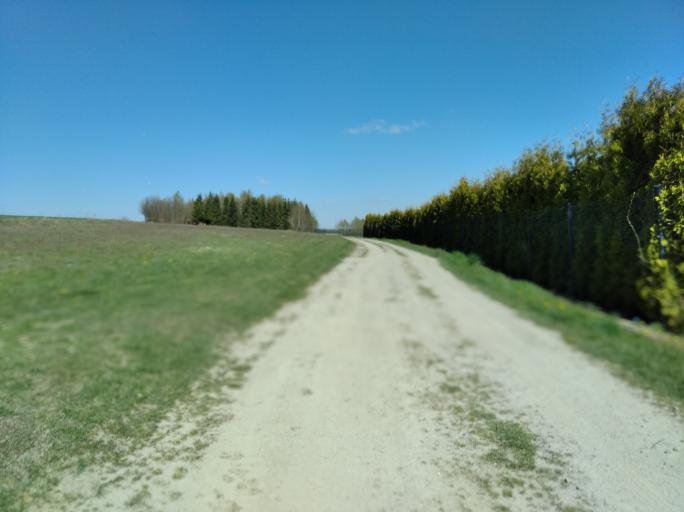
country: PL
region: Subcarpathian Voivodeship
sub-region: Powiat strzyzowski
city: Wisniowa
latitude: 49.9052
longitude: 21.6538
